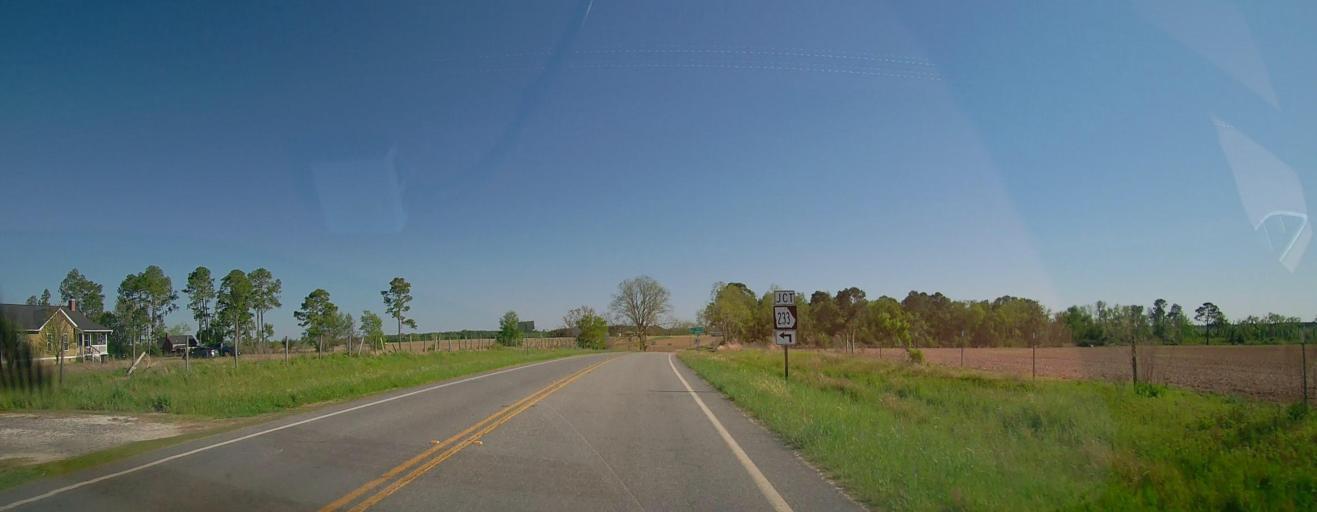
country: US
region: Georgia
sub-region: Wilcox County
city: Rochelle
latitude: 31.9782
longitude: -83.4567
